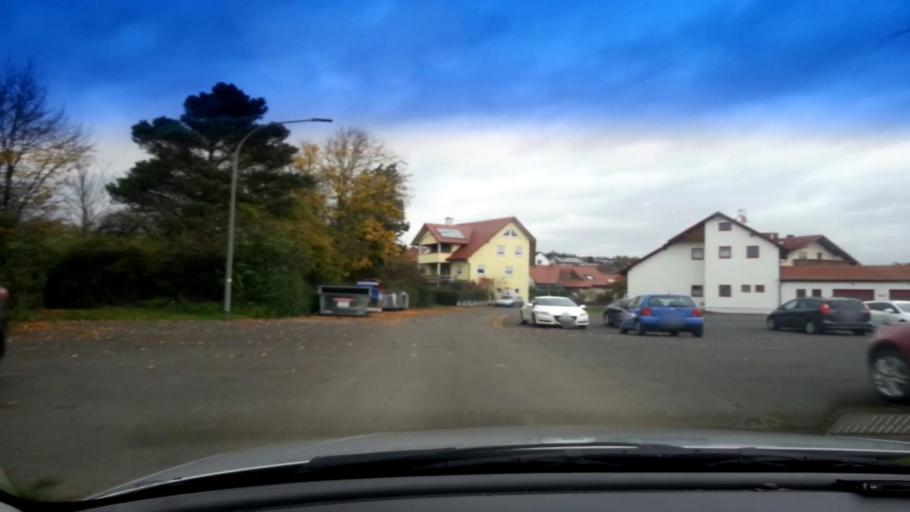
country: DE
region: Bavaria
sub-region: Upper Franconia
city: Hallstadt
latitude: 49.9299
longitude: 10.8539
